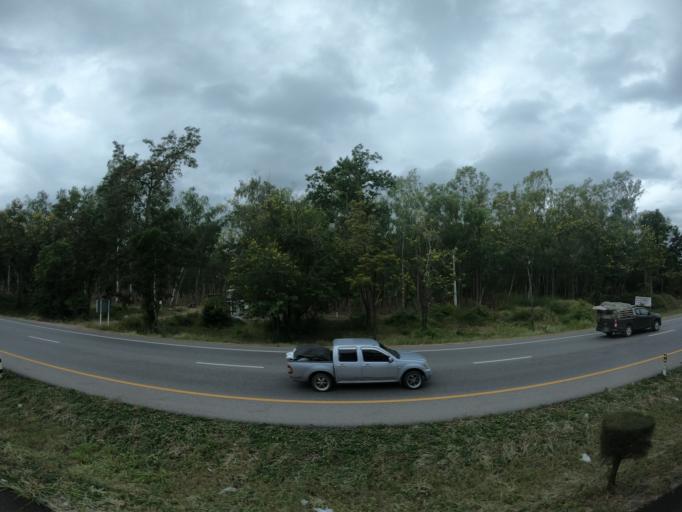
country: TH
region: Khon Kaen
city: Ban Phai
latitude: 16.0317
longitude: 102.7114
